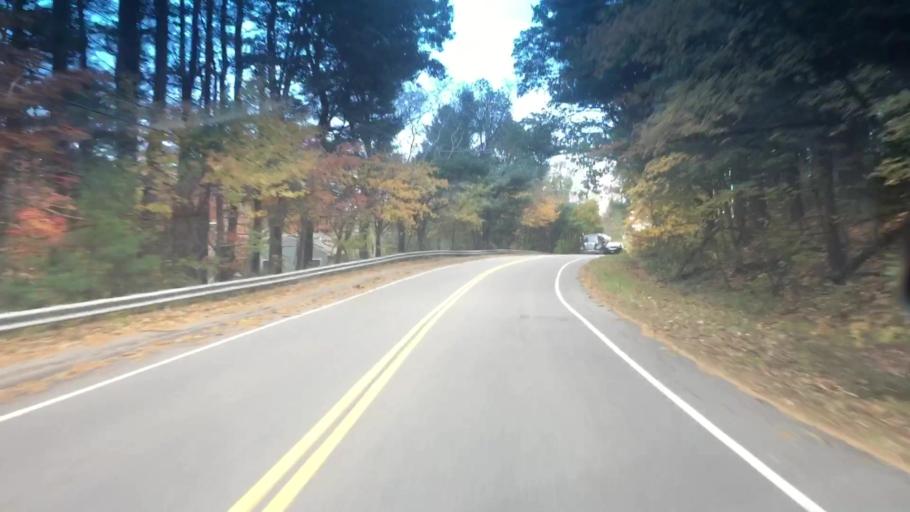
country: US
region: Massachusetts
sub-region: Norfolk County
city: Westwood
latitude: 42.2180
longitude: -71.2349
